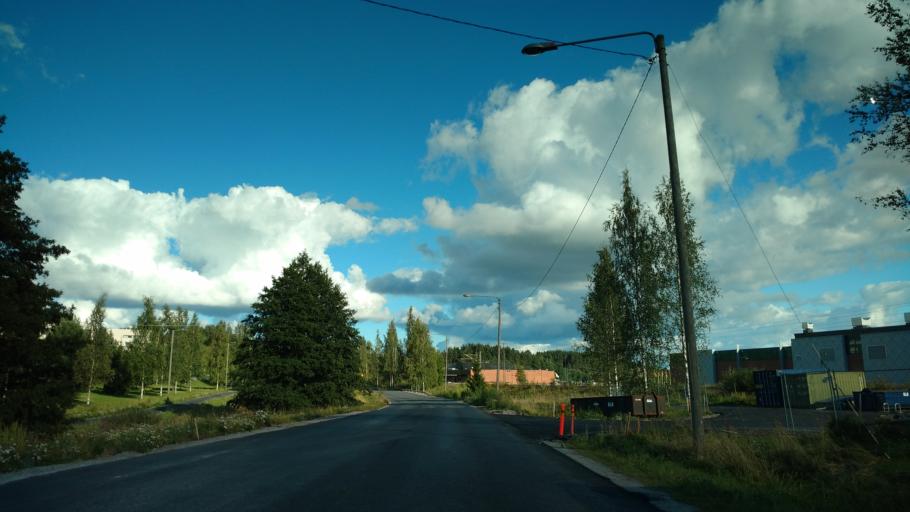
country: FI
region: Varsinais-Suomi
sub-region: Salo
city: Halikko
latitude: 60.3957
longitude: 23.0831
